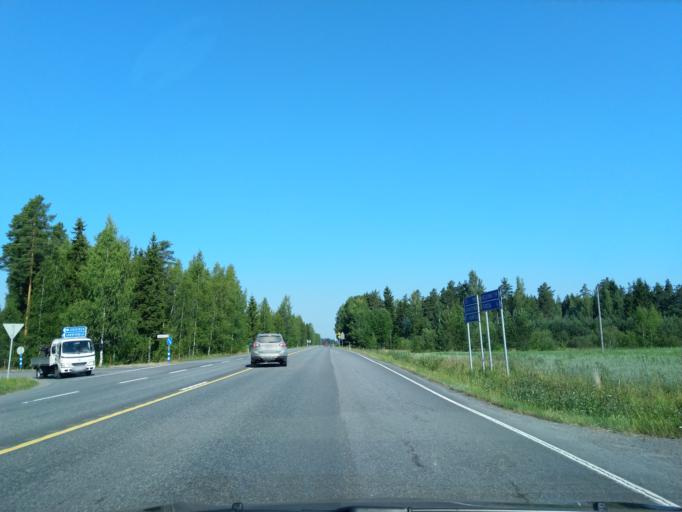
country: FI
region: Haeme
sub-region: Forssa
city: Forssa
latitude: 60.8328
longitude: 23.5574
